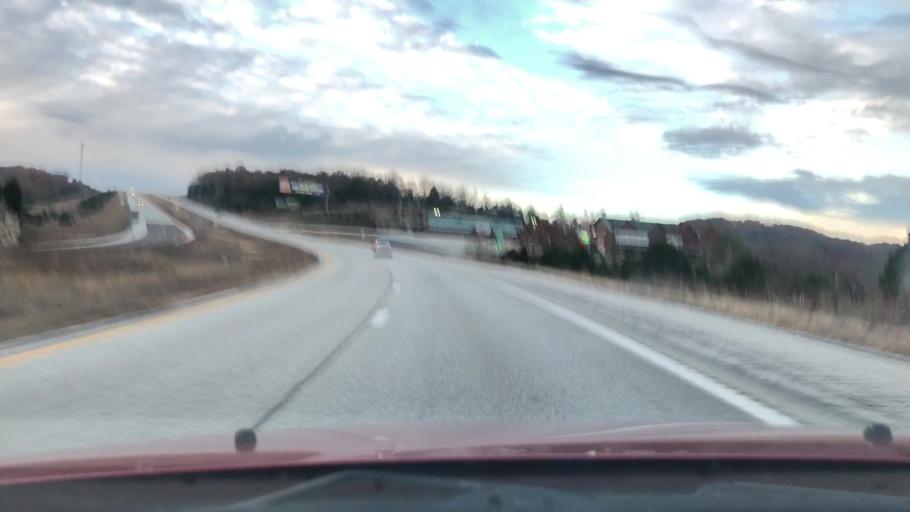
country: US
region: Missouri
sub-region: Taney County
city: Merriam Woods
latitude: 36.8223
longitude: -93.2263
